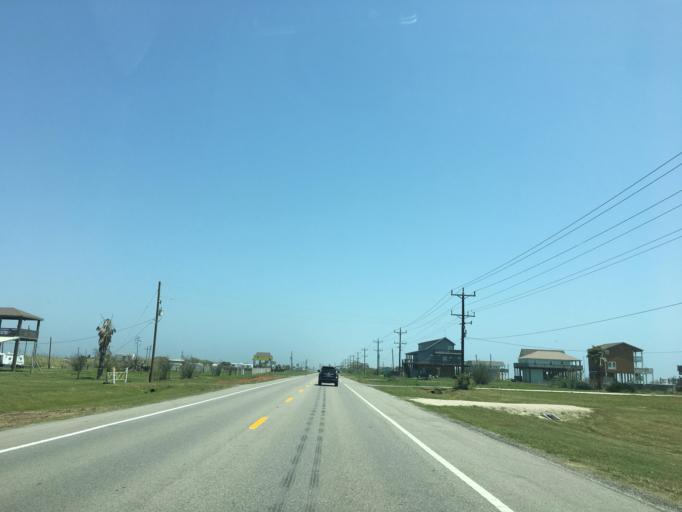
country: US
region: Texas
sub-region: Galveston County
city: Bolivar Peninsula
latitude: 29.4999
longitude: -94.5228
